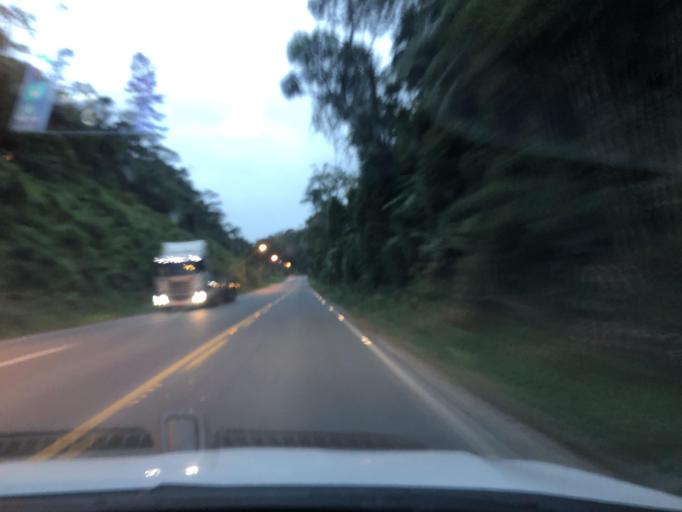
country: BR
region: Santa Catarina
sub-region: Pomerode
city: Pomerode
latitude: -26.7249
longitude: -49.0631
